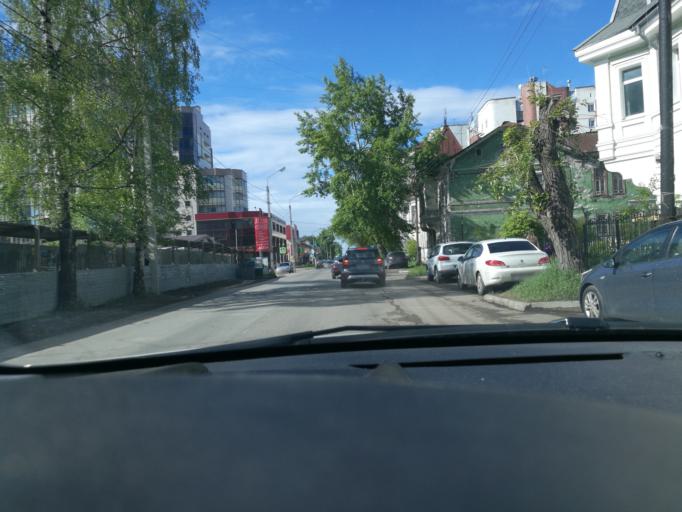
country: RU
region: Arkhangelskaya
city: Arkhangel'sk
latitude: 64.5378
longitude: 40.5301
